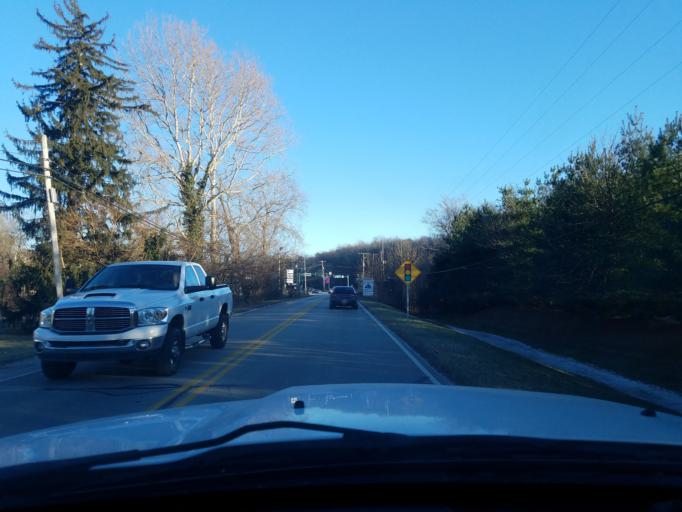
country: US
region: Indiana
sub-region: Floyd County
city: New Albany
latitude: 38.3250
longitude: -85.8758
